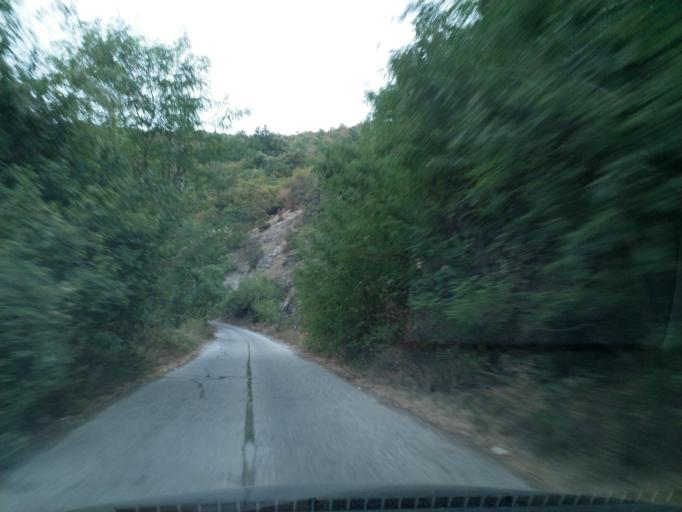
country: RS
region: Central Serbia
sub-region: Pomoravski Okrug
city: Paracin
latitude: 43.8671
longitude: 21.4593
